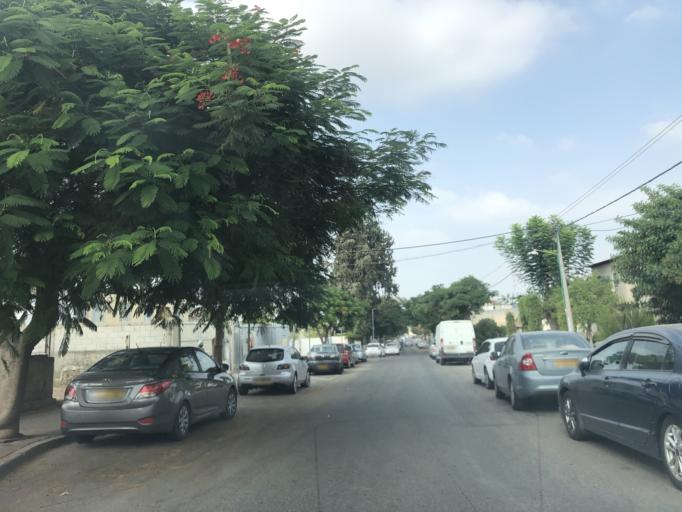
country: IL
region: Central District
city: Rosh Ha'Ayin
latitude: 32.0957
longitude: 34.9525
